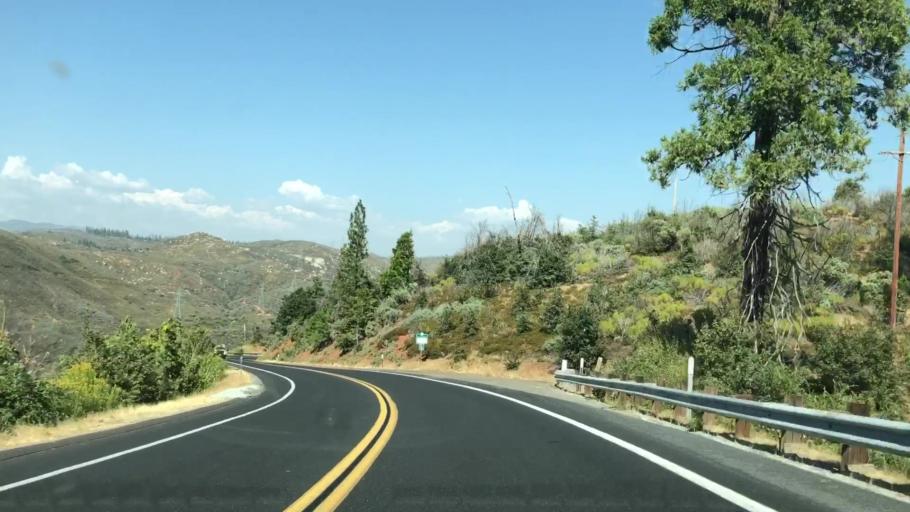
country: US
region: California
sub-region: Tuolumne County
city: Tuolumne City
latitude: 37.8231
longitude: -120.0224
